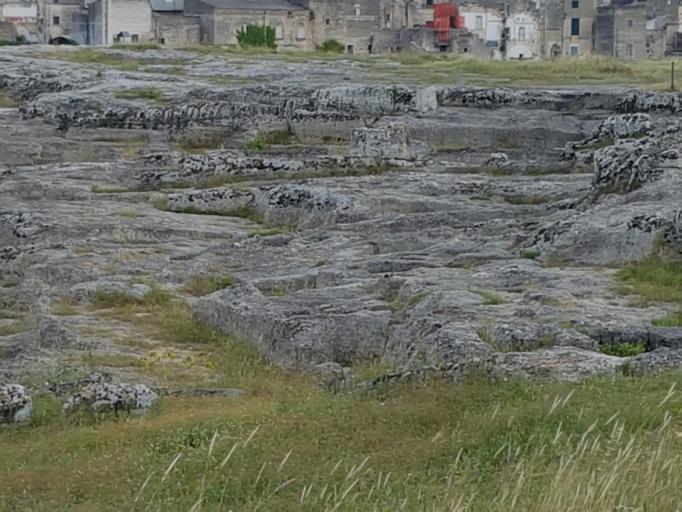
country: IT
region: Apulia
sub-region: Provincia di Bari
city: Gravina in Puglia
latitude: 40.8219
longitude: 16.4103
